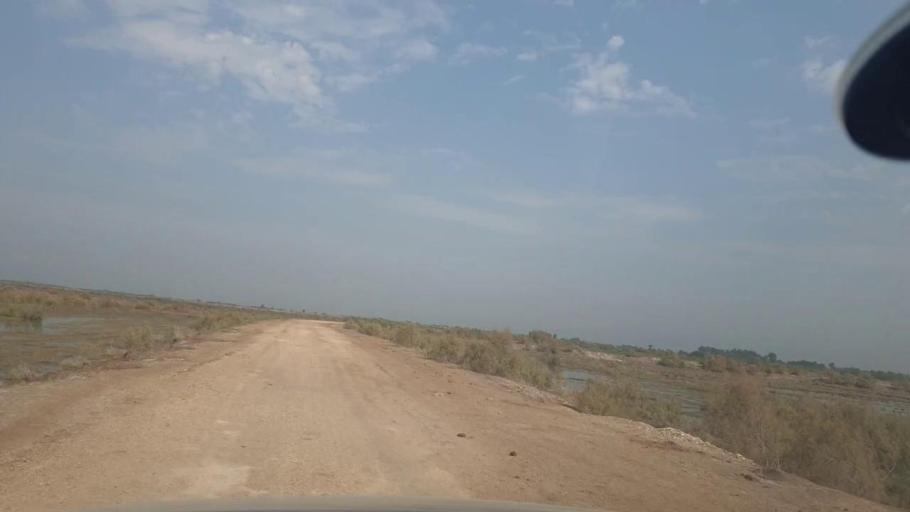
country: PK
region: Balochistan
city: Mehrabpur
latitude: 28.0425
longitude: 68.1226
